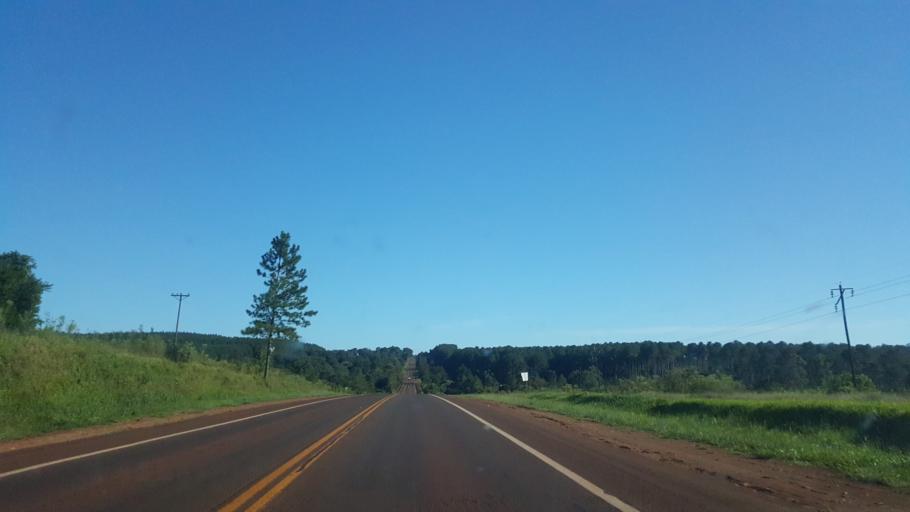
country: AR
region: Misiones
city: Puerto Esperanza
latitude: -26.1470
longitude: -54.5826
